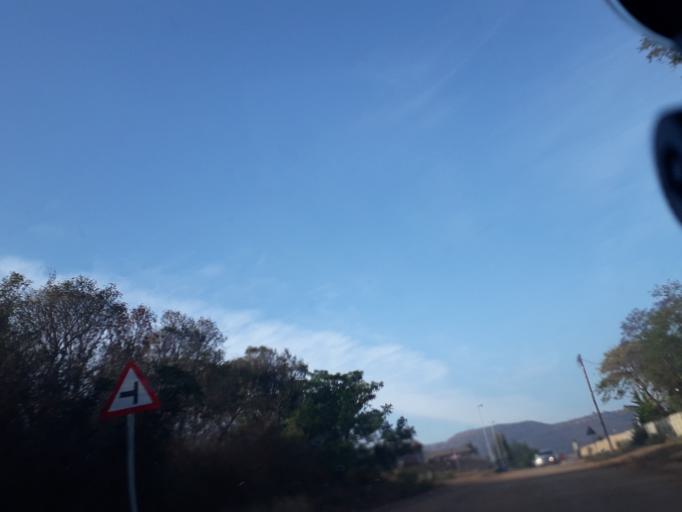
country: ZA
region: Gauteng
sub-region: City of Johannesburg Metropolitan Municipality
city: Roodepoort
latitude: -26.1002
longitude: 27.8945
